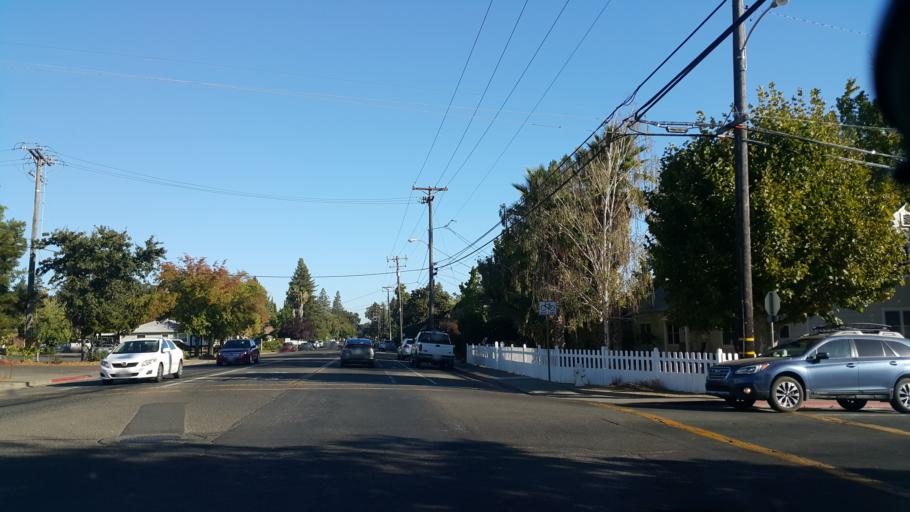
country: US
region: California
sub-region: Mendocino County
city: Ukiah
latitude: 39.1420
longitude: -123.2106
